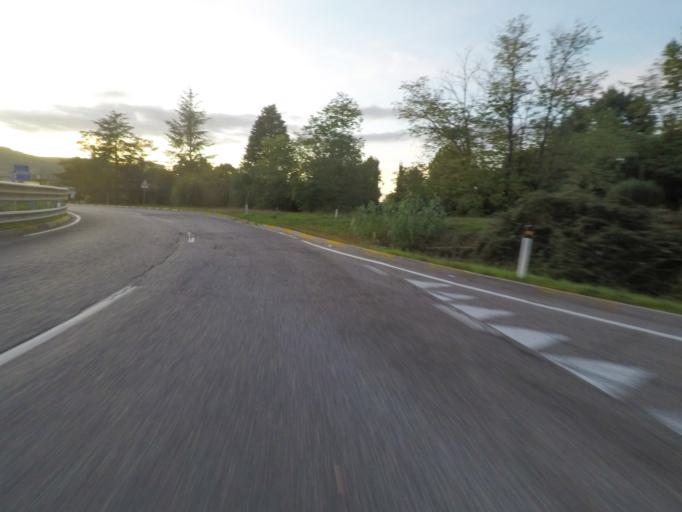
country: IT
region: Tuscany
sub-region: Provincia di Siena
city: Sinalunga
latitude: 43.2218
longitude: 11.7569
